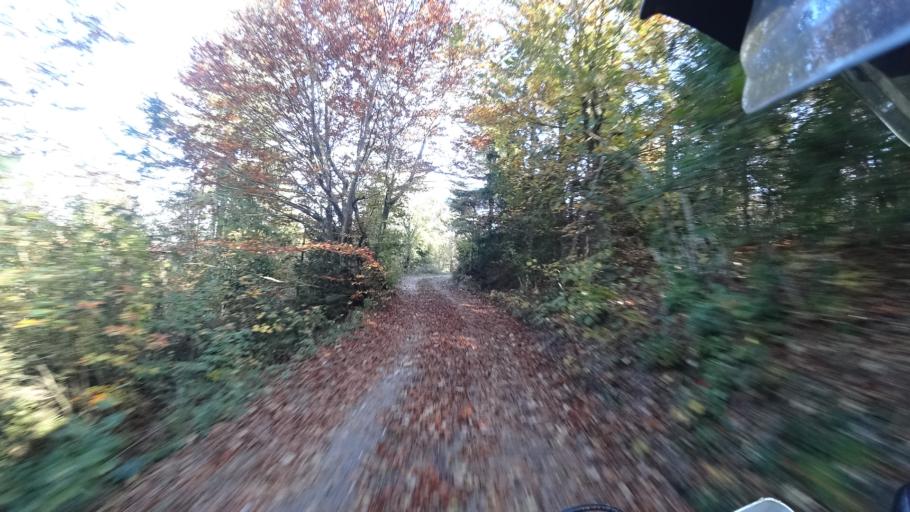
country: HR
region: Karlovacka
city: Plaski
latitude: 44.9986
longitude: 15.4069
